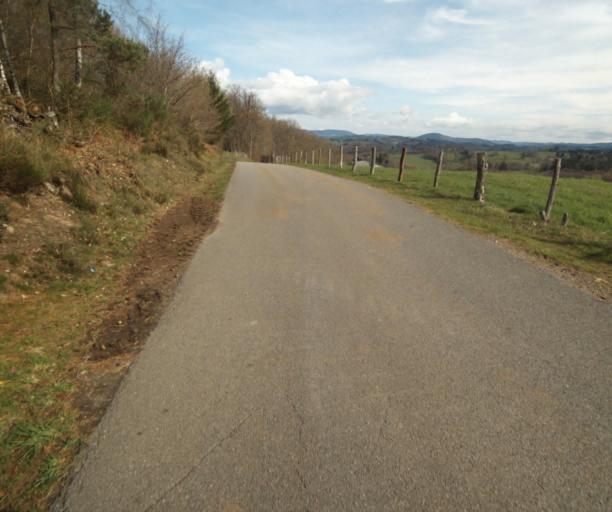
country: FR
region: Limousin
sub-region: Departement de la Correze
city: Correze
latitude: 45.3354
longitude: 1.8557
